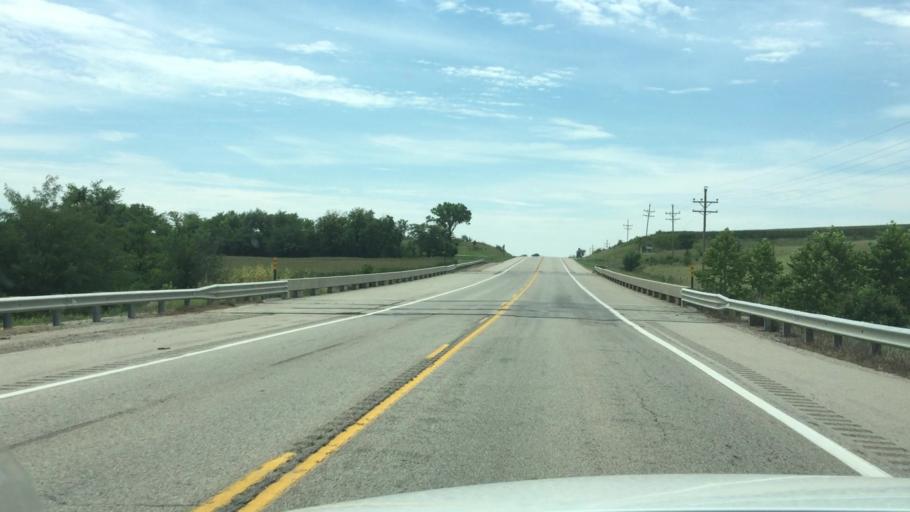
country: US
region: Kansas
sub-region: Nemaha County
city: Sabetha
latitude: 39.7998
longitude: -95.7294
